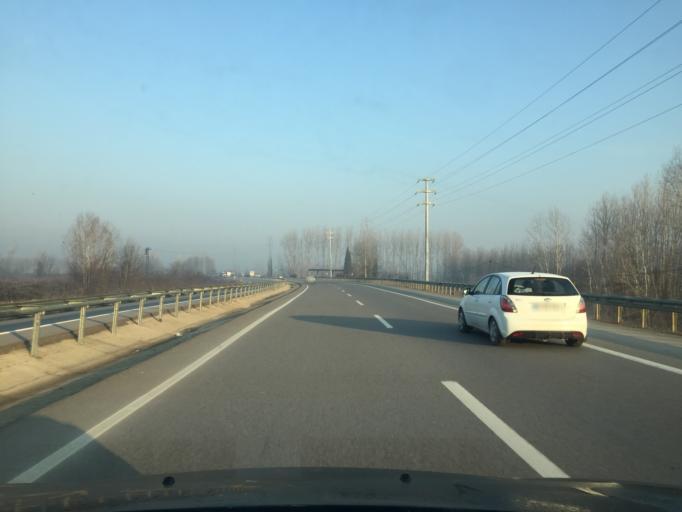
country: TR
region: Sakarya
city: Akyazi
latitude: 40.6922
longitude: 30.5733
